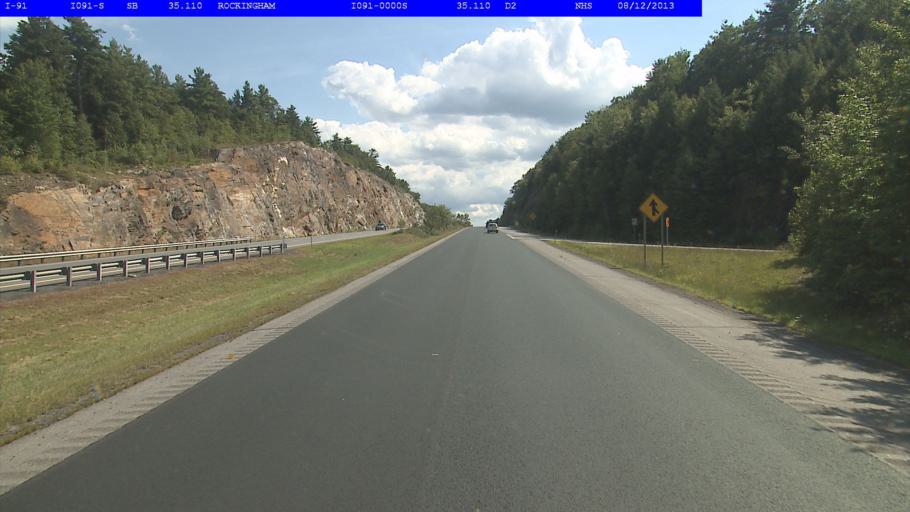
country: US
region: Vermont
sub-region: Windham County
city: Rockingham
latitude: 43.1776
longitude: -72.4632
